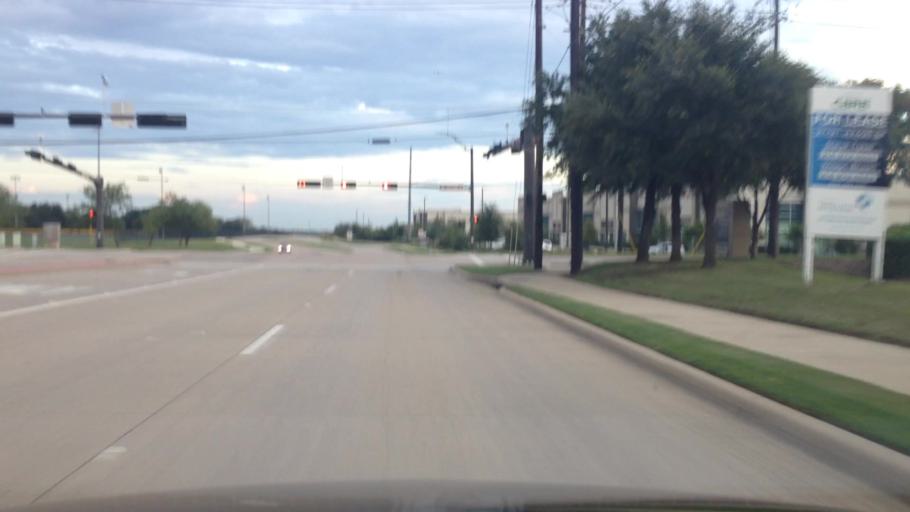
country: US
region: Texas
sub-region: Denton County
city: Flower Mound
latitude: 32.9986
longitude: -97.0471
